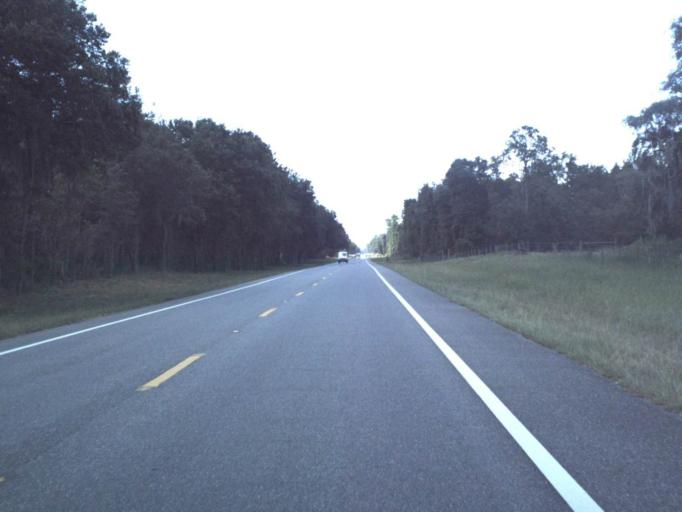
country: US
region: Florida
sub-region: Alachua County
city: High Springs
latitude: 29.8195
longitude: -82.7414
